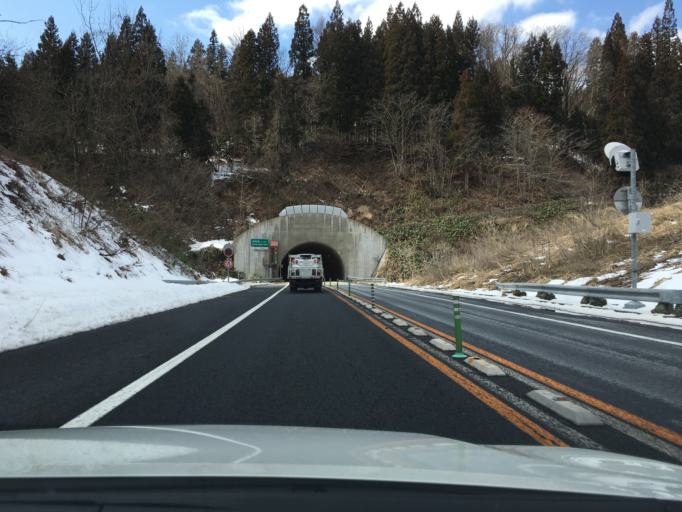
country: JP
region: Yamagata
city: Sagae
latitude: 38.4392
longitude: 140.1223
